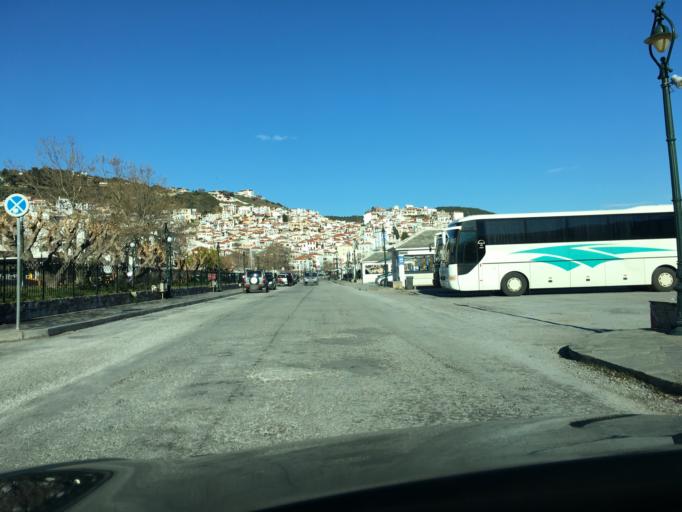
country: GR
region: Thessaly
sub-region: Nomos Magnisias
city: Skopelos
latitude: 39.1201
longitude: 23.7303
